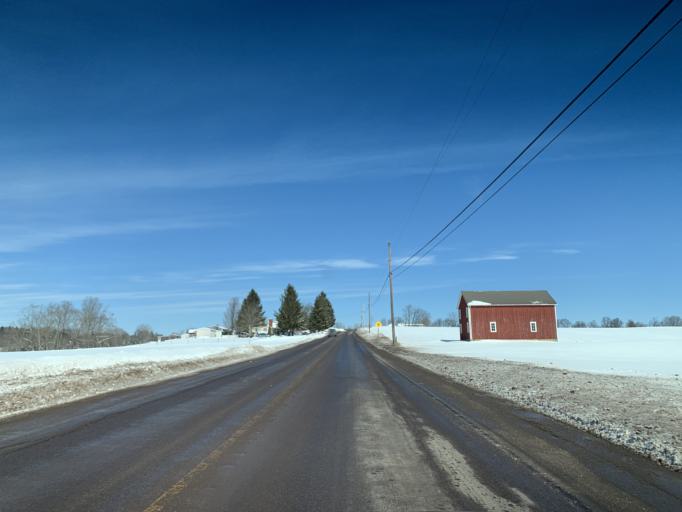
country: US
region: Pennsylvania
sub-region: Somerset County
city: Meyersdale
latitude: 39.7096
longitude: -79.1607
